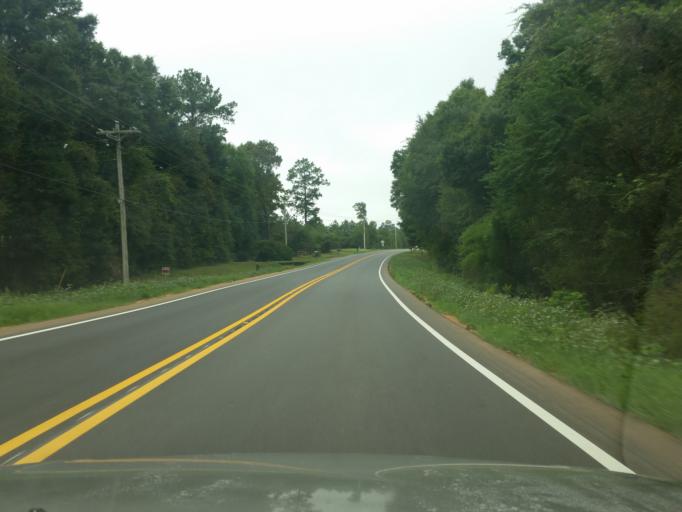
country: US
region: Alabama
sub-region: Baldwin County
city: Spanish Fort
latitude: 30.7436
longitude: -87.8938
